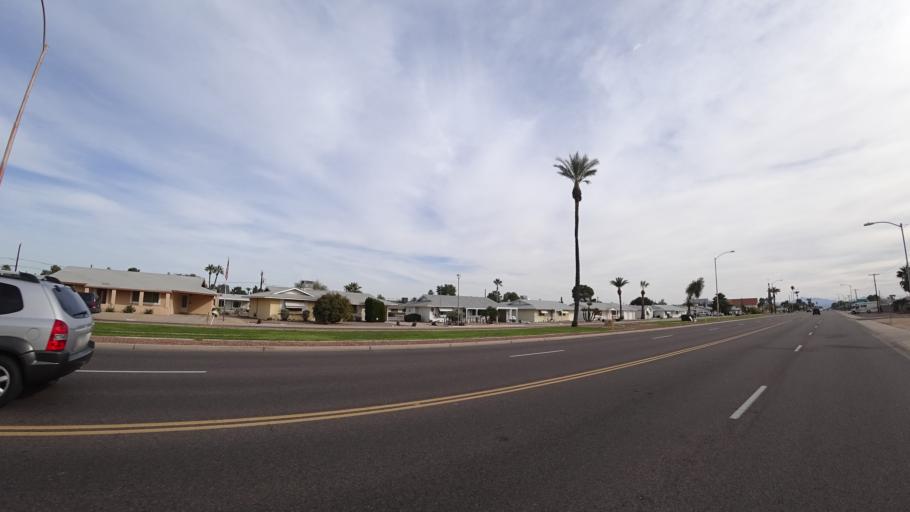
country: US
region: Arizona
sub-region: Maricopa County
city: Youngtown
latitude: 33.5878
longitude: -112.2988
